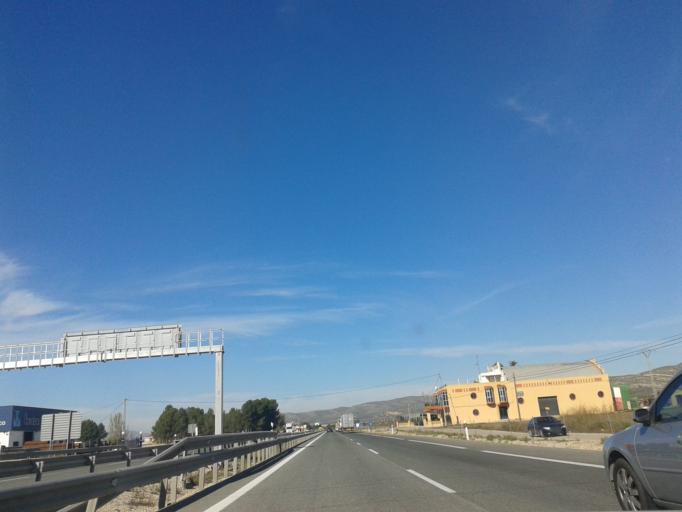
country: ES
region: Valencia
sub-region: Provincia de Alicante
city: Villena
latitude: 38.6549
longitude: -0.8752
